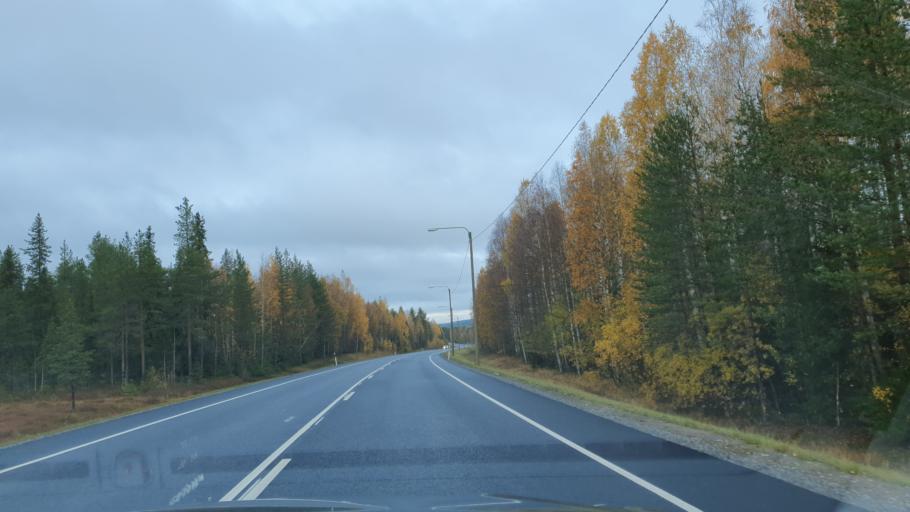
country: FI
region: Lapland
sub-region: Rovaniemi
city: Rovaniemi
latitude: 66.5391
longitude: 25.6593
